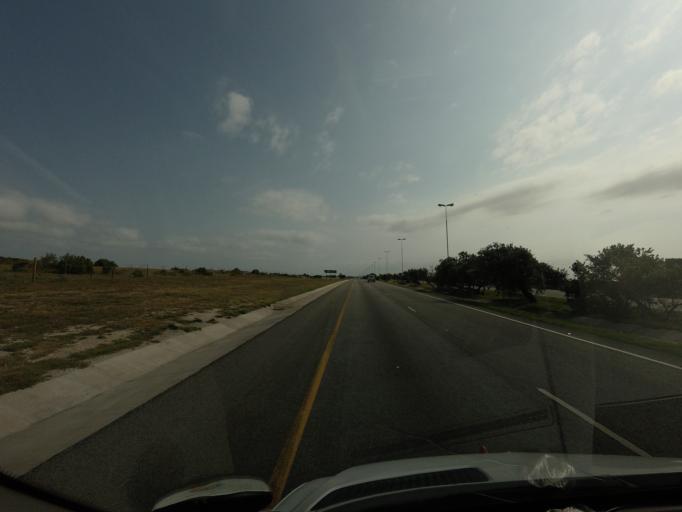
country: ZA
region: Eastern Cape
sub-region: Nelson Mandela Bay Metropolitan Municipality
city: Port Elizabeth
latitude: -33.8317
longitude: 25.6435
